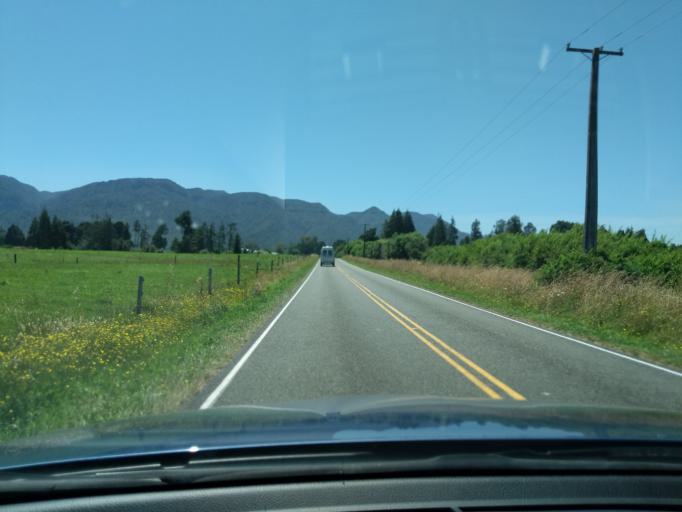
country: NZ
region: Tasman
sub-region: Tasman District
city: Takaka
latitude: -40.7113
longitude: 172.6373
